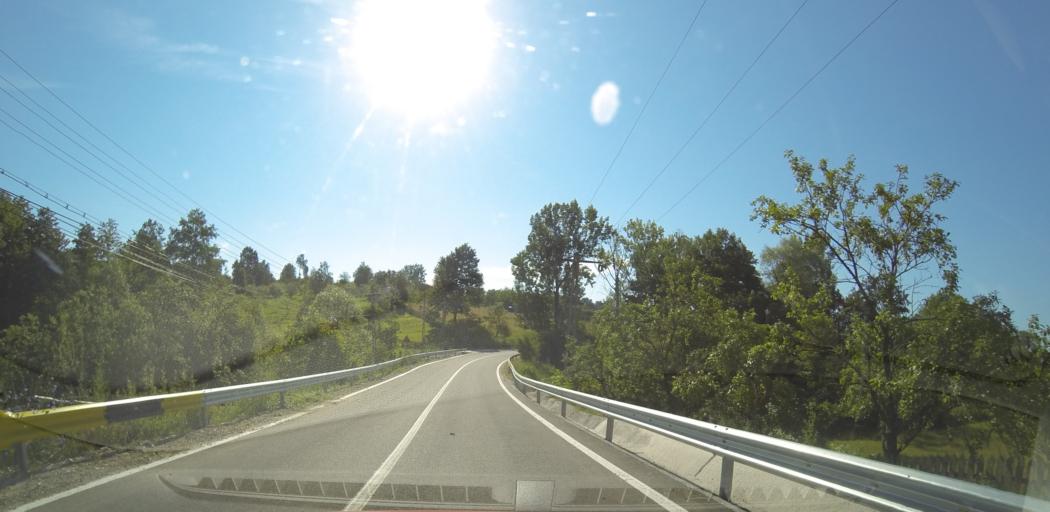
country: RO
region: Valcea
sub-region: Comuna Vaideeni
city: Vaideeni
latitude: 45.1690
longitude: 23.8791
